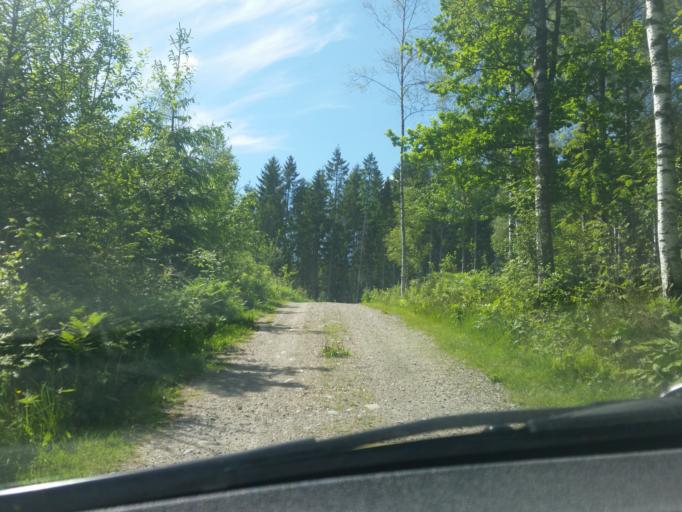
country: SE
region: Vaestra Goetaland
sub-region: Fargelanda Kommun
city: Faergelanda
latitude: 58.5868
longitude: 12.0292
